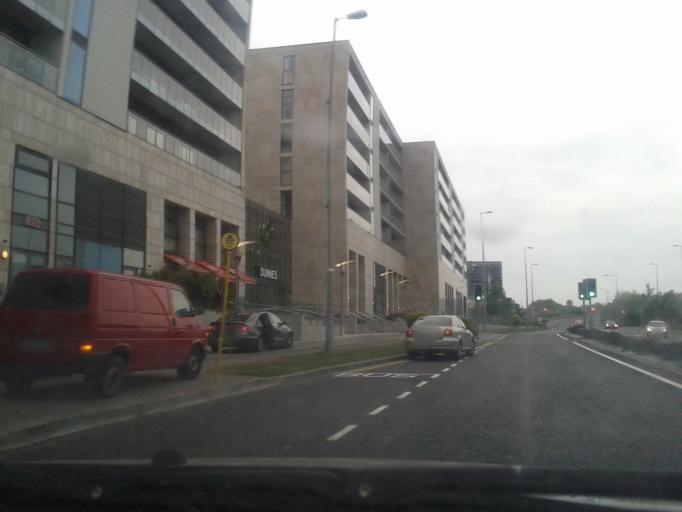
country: IE
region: Leinster
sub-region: Dublin City
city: Finglas
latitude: 53.4034
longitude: -6.3023
